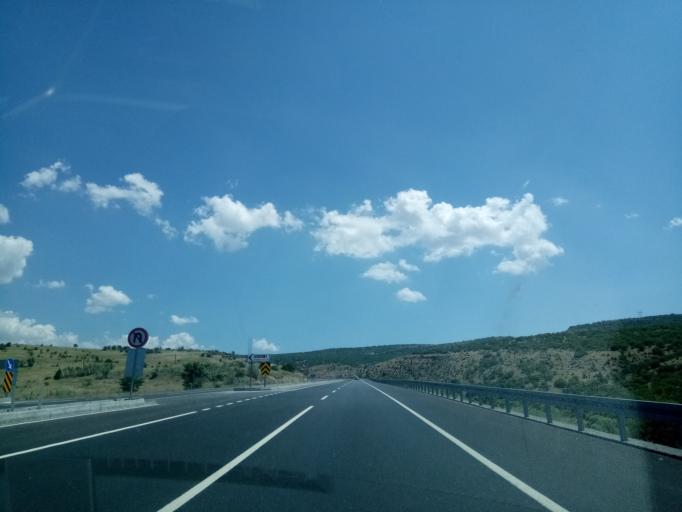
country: TR
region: Konya
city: Cavus
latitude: 37.6453
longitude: 31.9488
